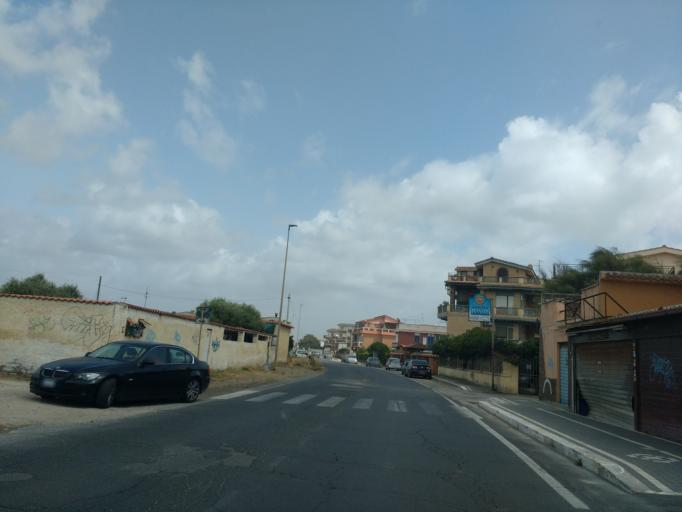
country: IT
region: Latium
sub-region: Citta metropolitana di Roma Capitale
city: Ardea
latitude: 41.5816
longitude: 12.5046
